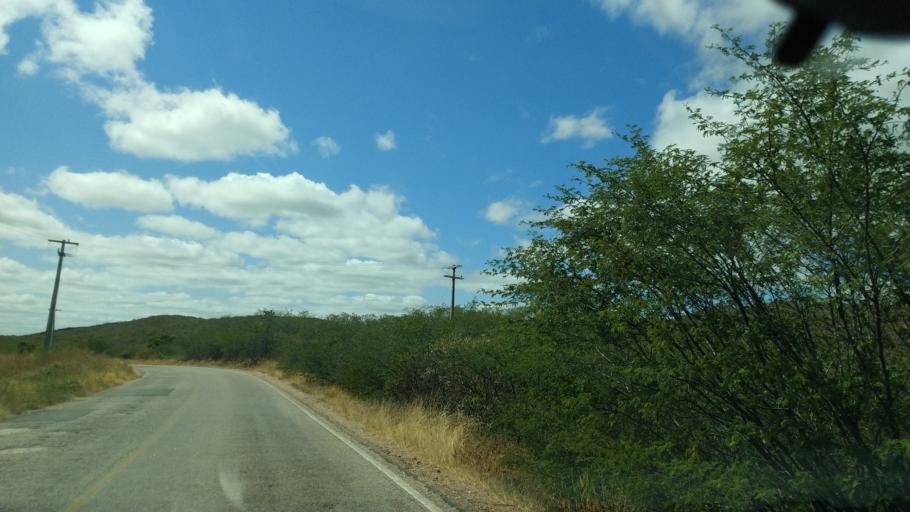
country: BR
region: Rio Grande do Norte
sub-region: Currais Novos
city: Currais Novos
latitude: -6.2644
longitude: -36.5905
